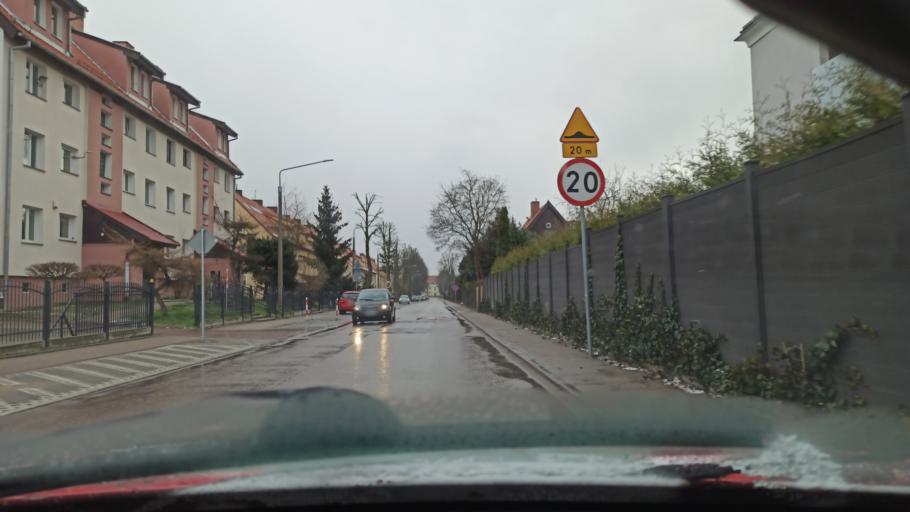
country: PL
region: Warmian-Masurian Voivodeship
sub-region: Powiat elblaski
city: Elblag
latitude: 54.1773
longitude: 19.4130
